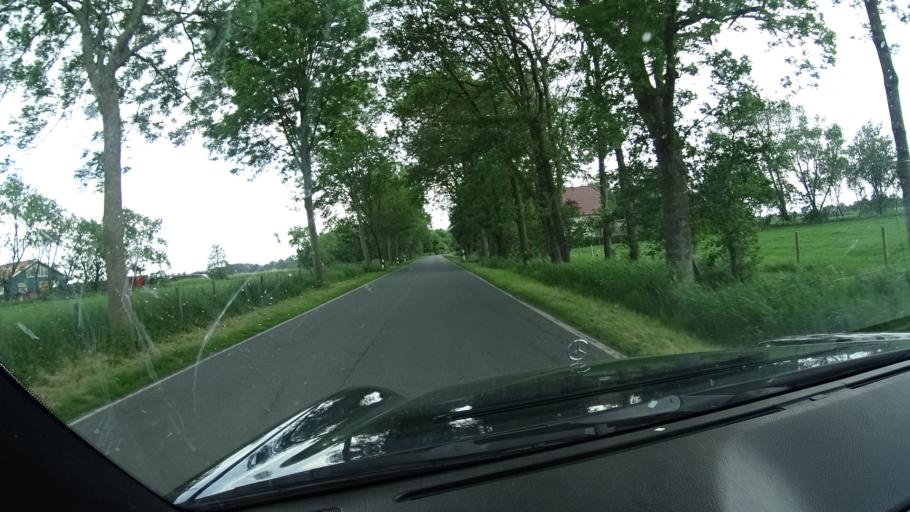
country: DE
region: Lower Saxony
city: Butjadingen
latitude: 53.5785
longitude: 8.2668
